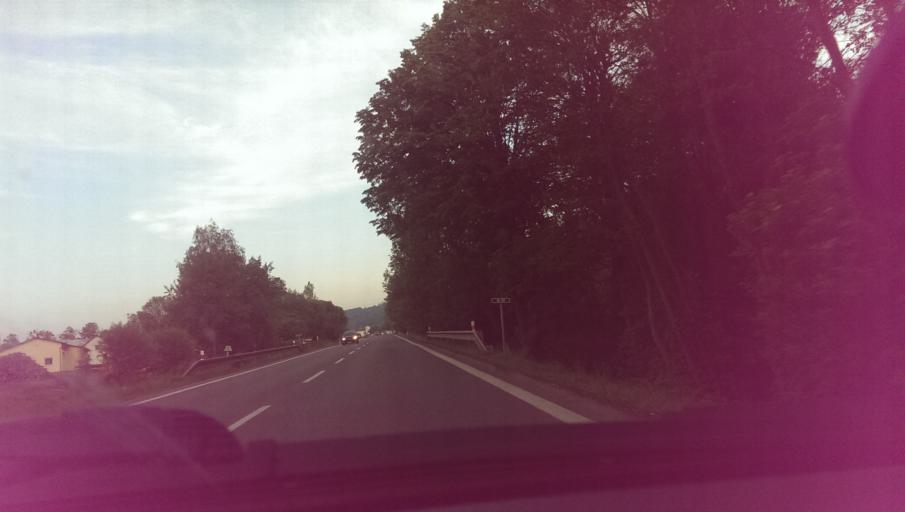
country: CZ
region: Zlin
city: Zasova
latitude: 49.4644
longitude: 18.0668
